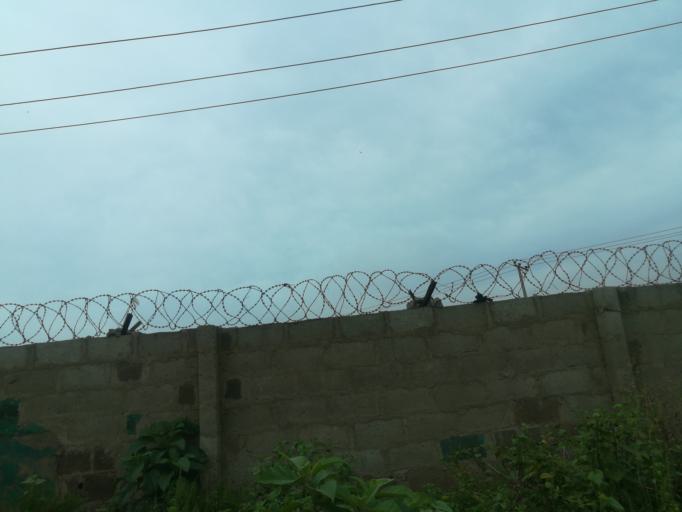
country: NG
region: Oyo
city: Ibadan
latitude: 7.3637
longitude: 3.9277
